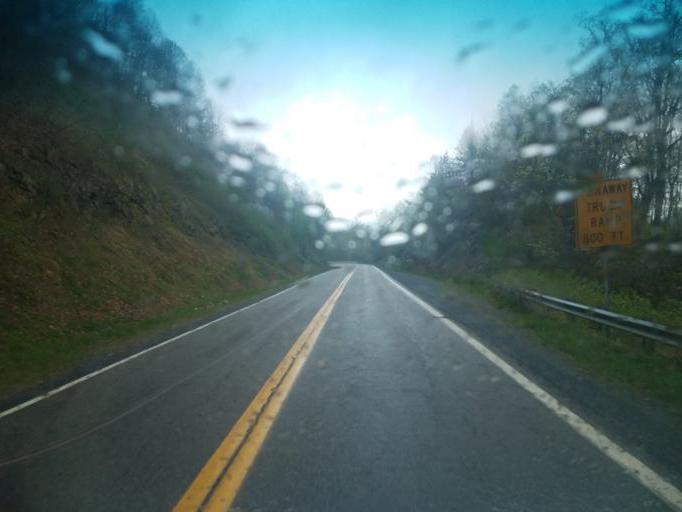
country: US
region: Virginia
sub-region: Smyth County
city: Adwolf
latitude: 36.7088
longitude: -81.6177
